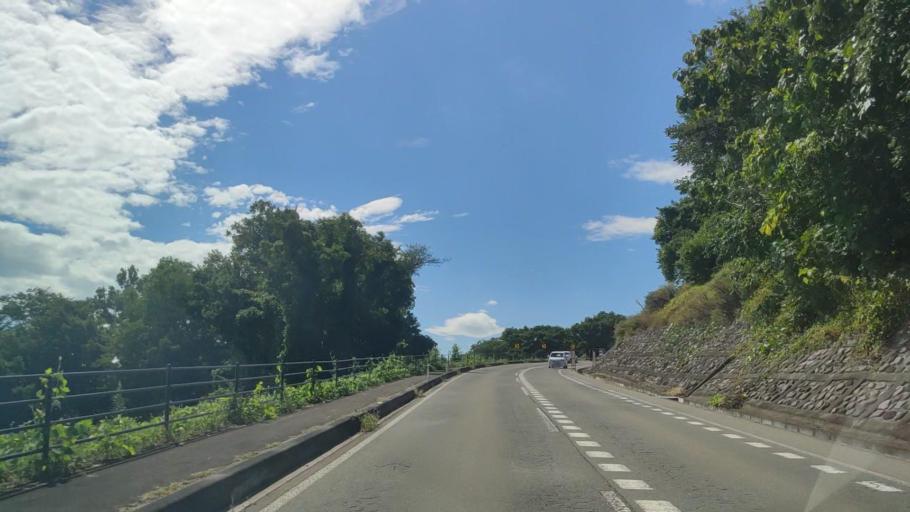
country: JP
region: Nagano
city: Suzaka
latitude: 36.7198
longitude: 138.2760
